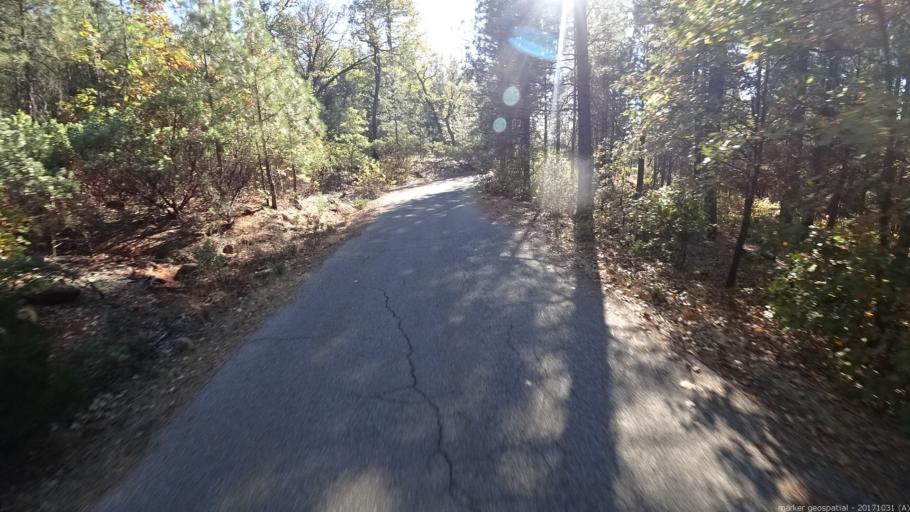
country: US
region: California
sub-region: Shasta County
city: Shingletown
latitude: 40.4850
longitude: -121.9279
